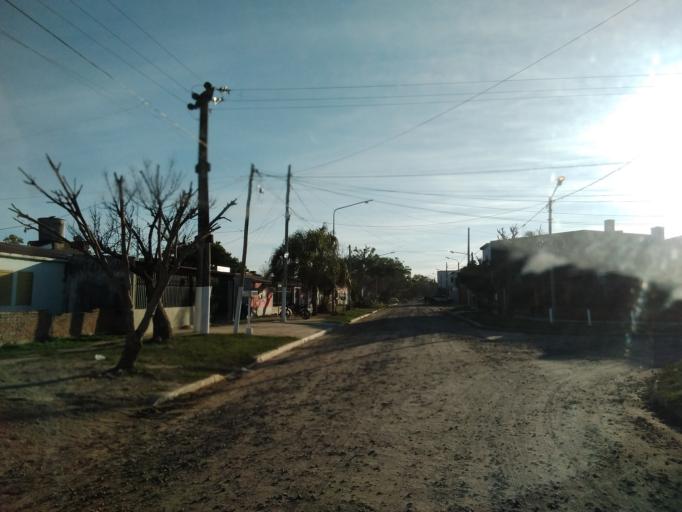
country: AR
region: Corrientes
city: Corrientes
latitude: -27.5014
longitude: -58.8333
